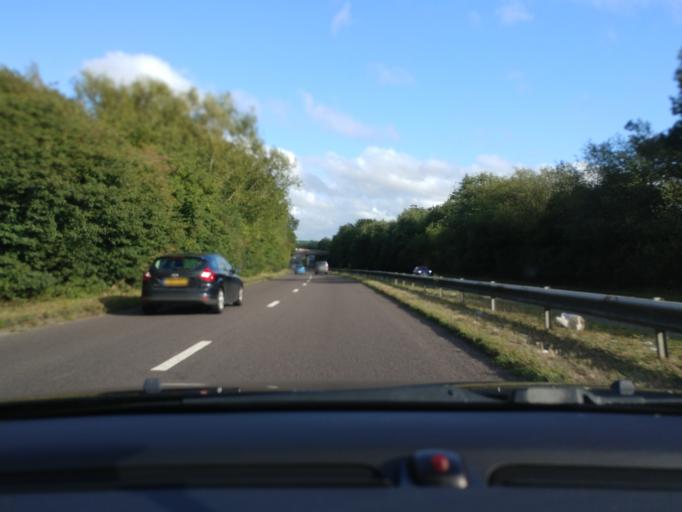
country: GB
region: England
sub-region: Oxfordshire
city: Cowley
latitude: 51.7181
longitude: -1.2316
